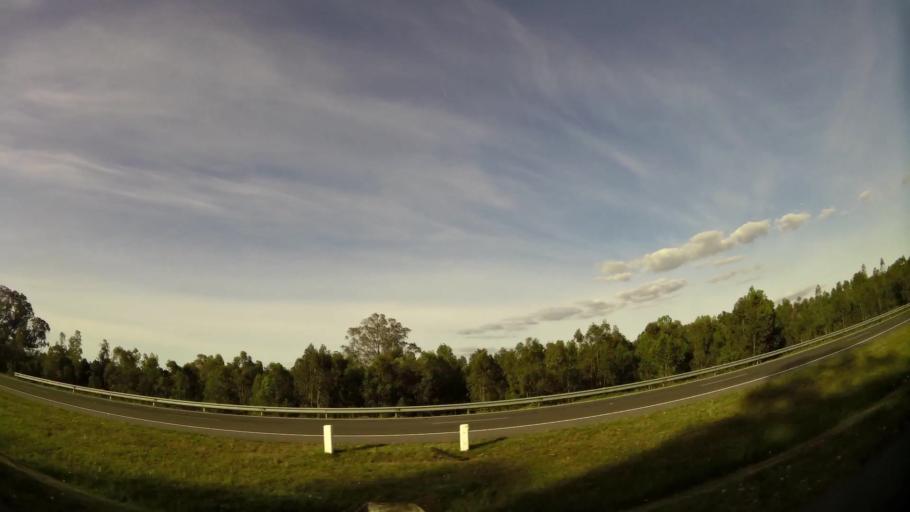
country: UY
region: Maldonado
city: Piriapolis
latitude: -34.7778
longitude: -55.3871
